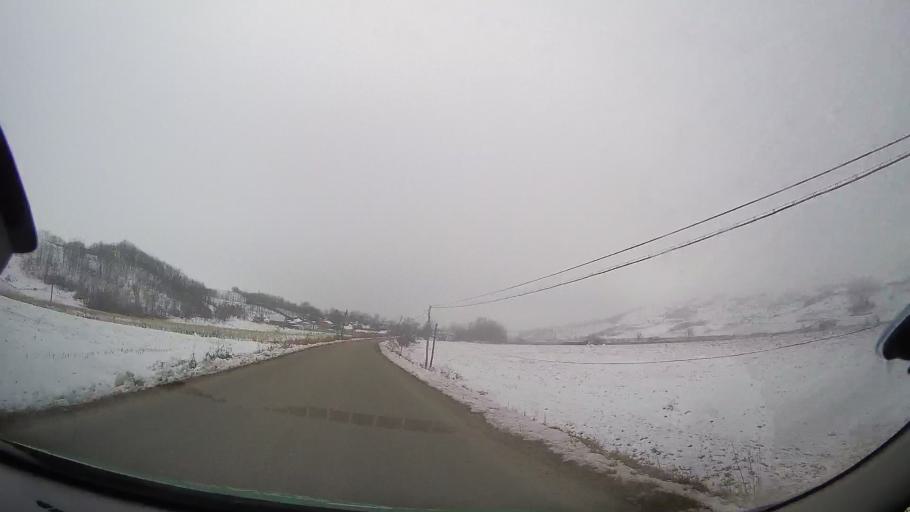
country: RO
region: Bacau
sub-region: Comuna Glavanesti
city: Frumuselu
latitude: 46.2924
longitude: 27.3009
